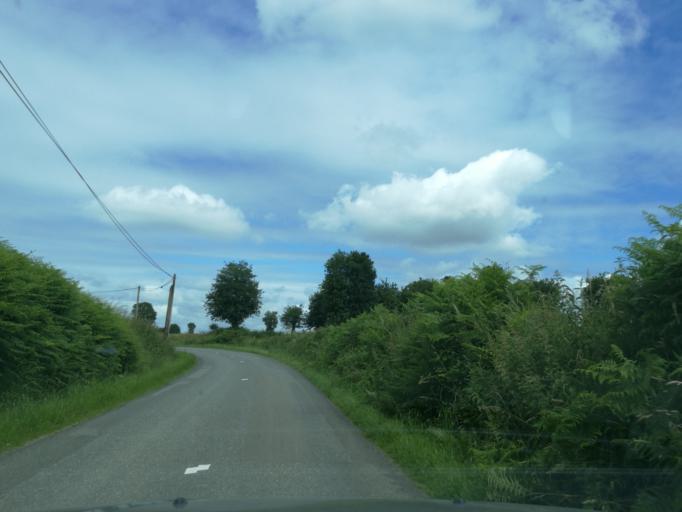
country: FR
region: Brittany
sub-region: Departement d'Ille-et-Vilaine
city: Bedee
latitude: 48.1952
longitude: -1.9887
